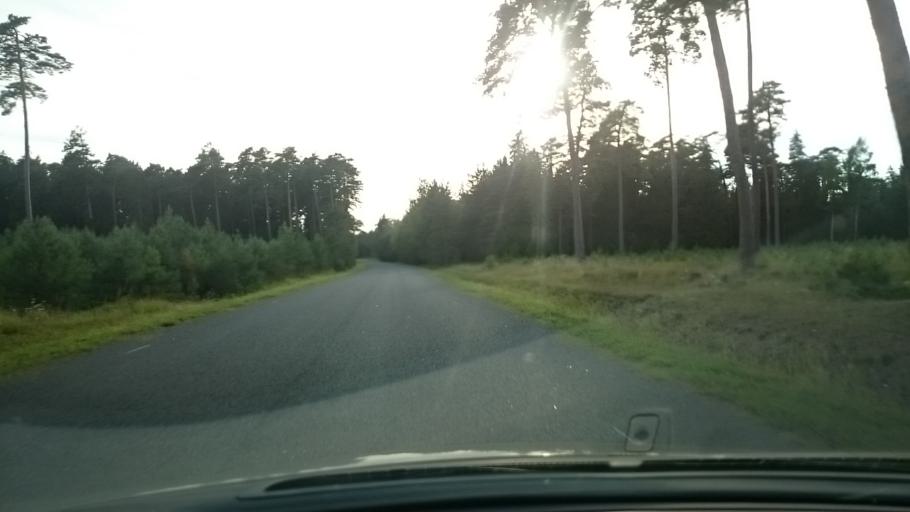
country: EE
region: Saare
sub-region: Kuressaare linn
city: Kuressaare
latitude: 58.4306
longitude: 22.2012
